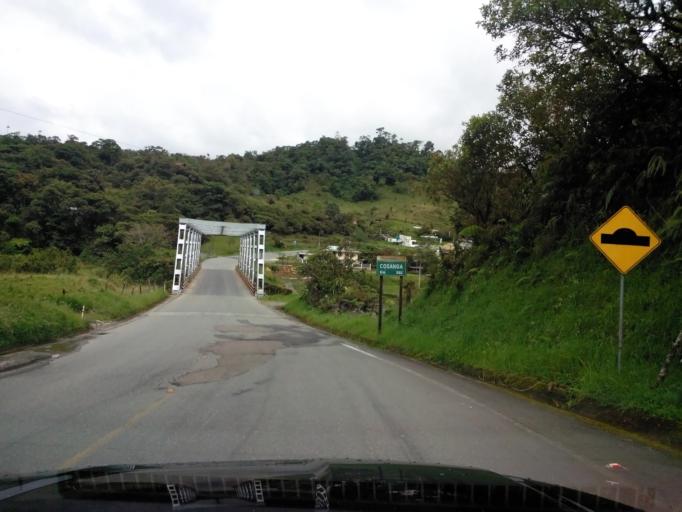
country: EC
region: Napo
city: Archidona
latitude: -0.5800
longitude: -77.8645
